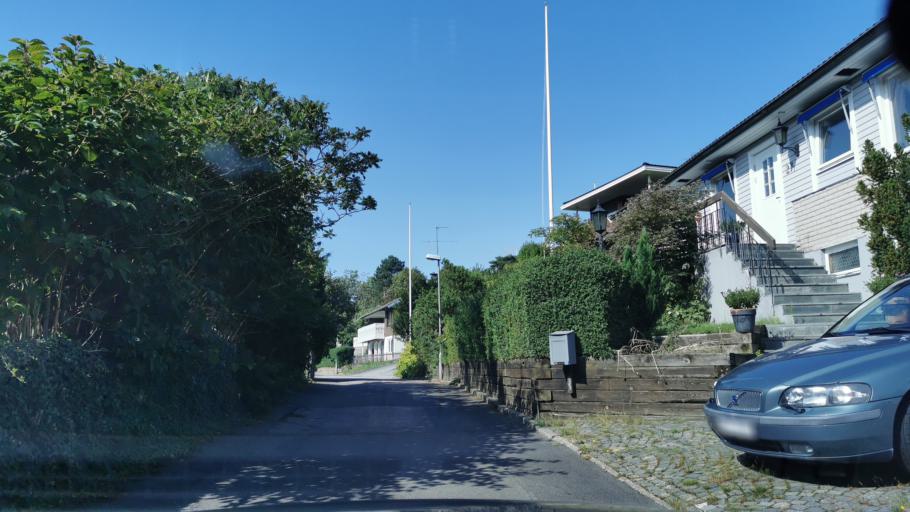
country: SE
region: Vaestra Goetaland
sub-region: Goteborg
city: Majorna
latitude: 57.6385
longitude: 11.9079
